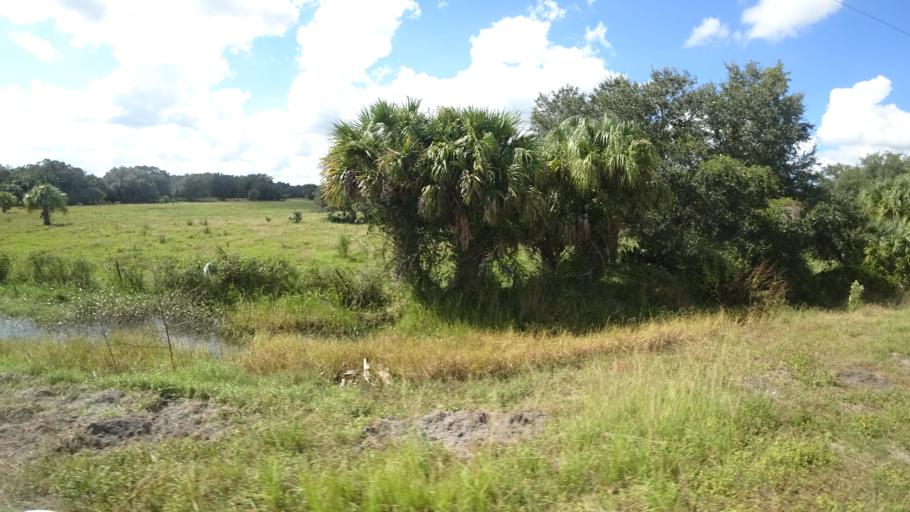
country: US
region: Florida
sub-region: Sarasota County
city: North Port
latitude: 27.2131
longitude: -82.1221
